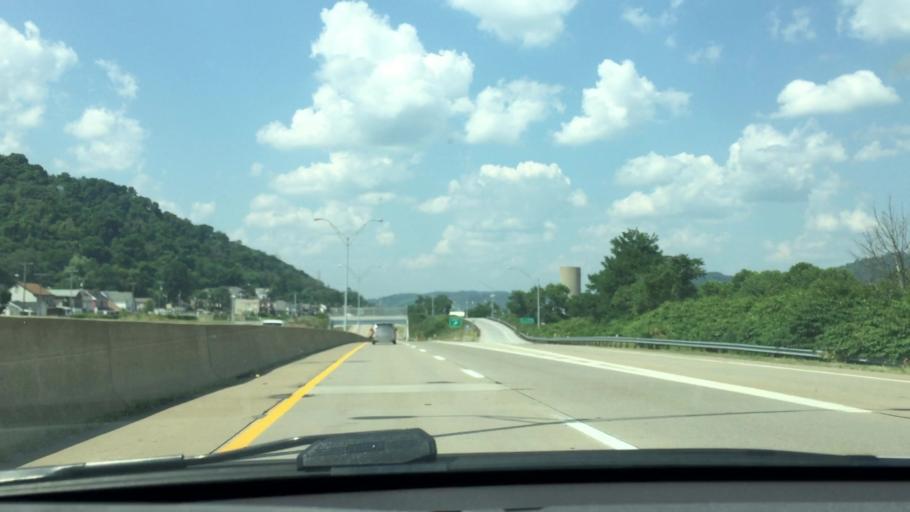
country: US
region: West Virginia
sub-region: Marshall County
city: Benwood
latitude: 40.0276
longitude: -80.7388
